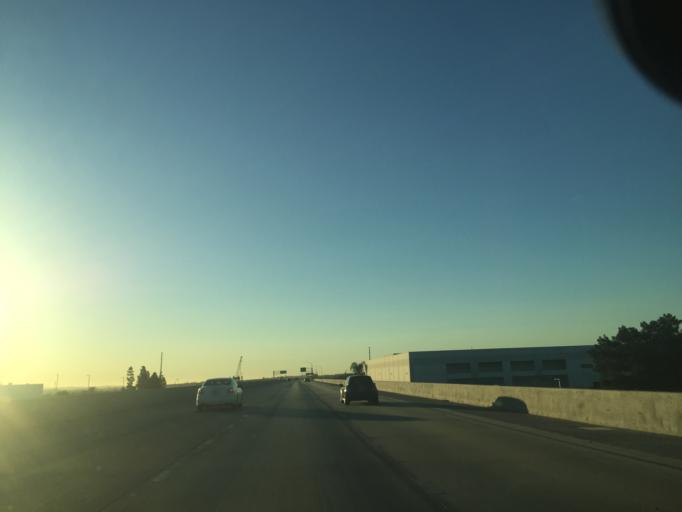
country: MX
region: Baja California
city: Tijuana
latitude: 32.5641
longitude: -116.9379
